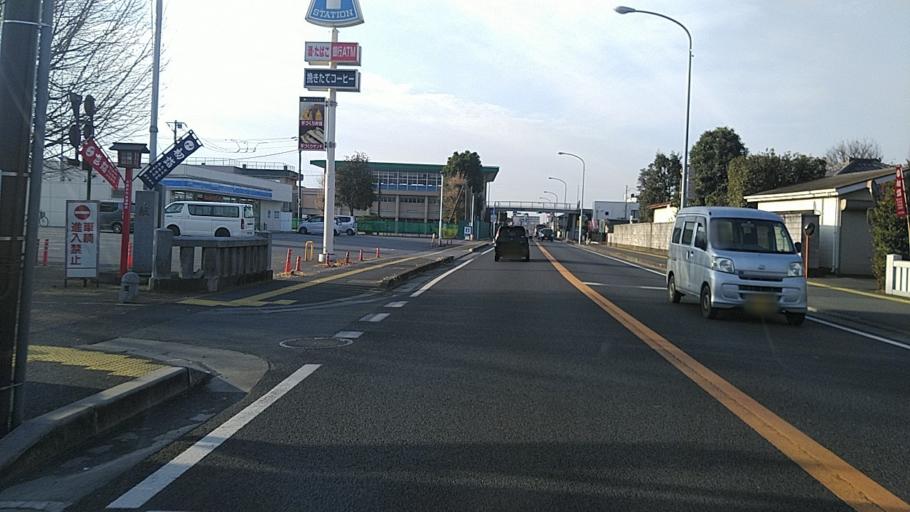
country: JP
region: Tochigi
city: Oyama
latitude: 36.3116
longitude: 139.7997
